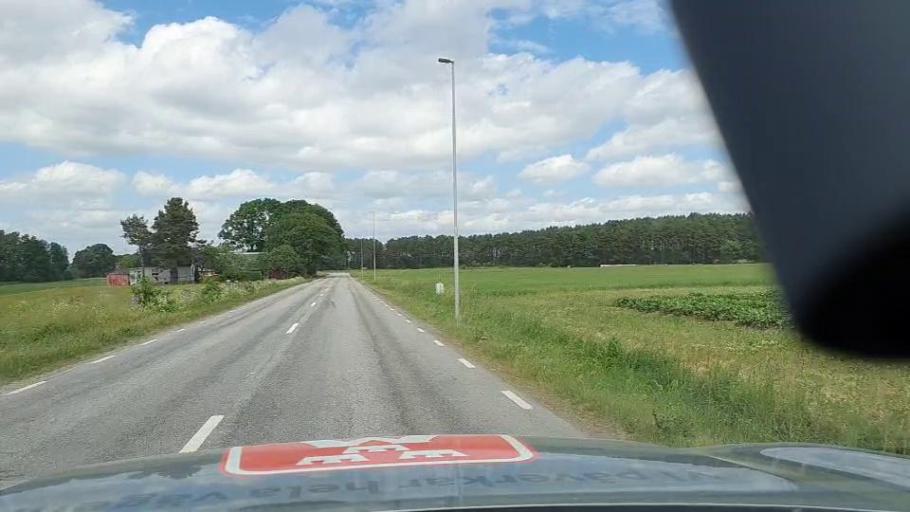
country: SE
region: Blekinge
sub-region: Karlshamns Kommun
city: Morrum
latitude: 56.0867
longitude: 14.7049
